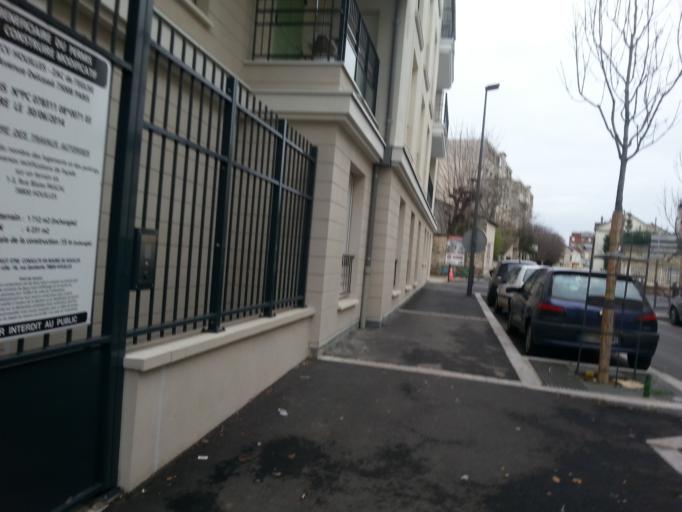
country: FR
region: Ile-de-France
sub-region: Departement des Yvelines
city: Houilles
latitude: 48.9266
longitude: 2.1885
